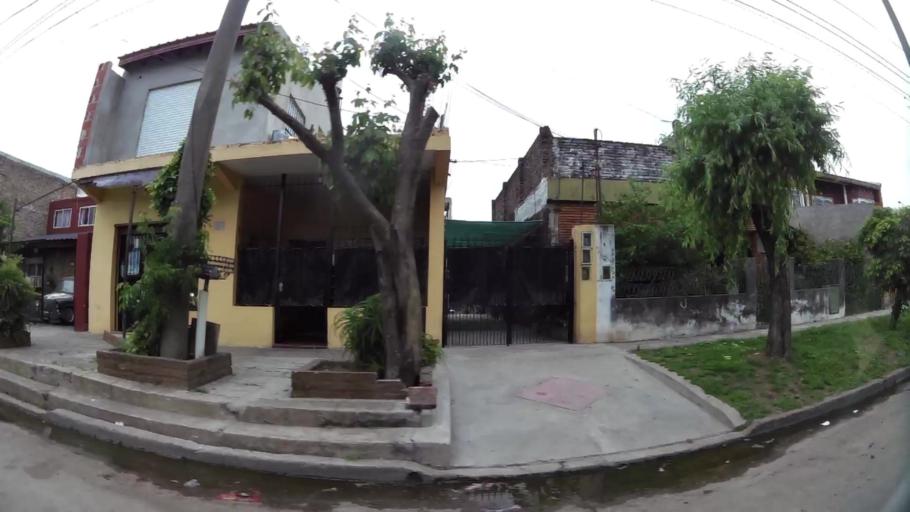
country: AR
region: Buenos Aires
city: San Justo
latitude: -34.7018
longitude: -58.5568
